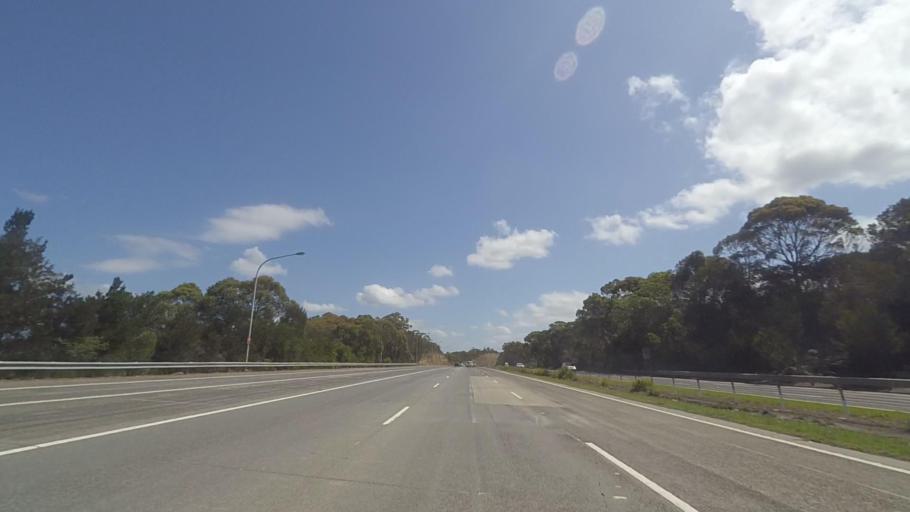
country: AU
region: New South Wales
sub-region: Hornsby Shire
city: Berowra
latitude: -33.6375
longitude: 151.1467
